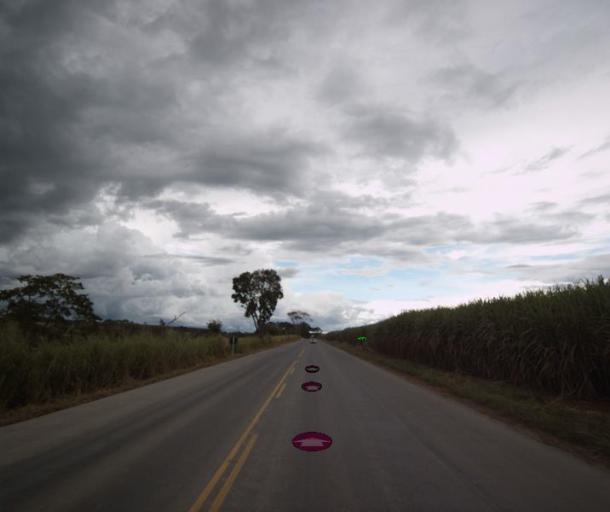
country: BR
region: Goias
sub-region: Itapaci
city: Itapaci
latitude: -14.9822
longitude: -49.3986
